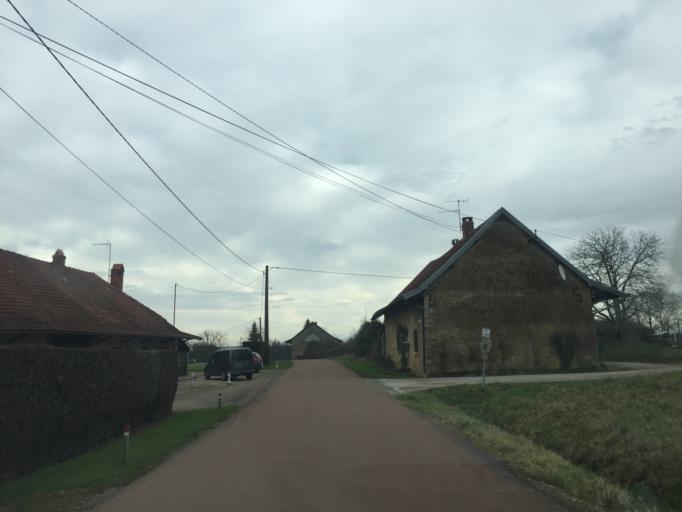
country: FR
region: Franche-Comte
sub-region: Departement du Jura
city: Mont-sous-Vaudrey
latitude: 46.8656
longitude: 5.5323
